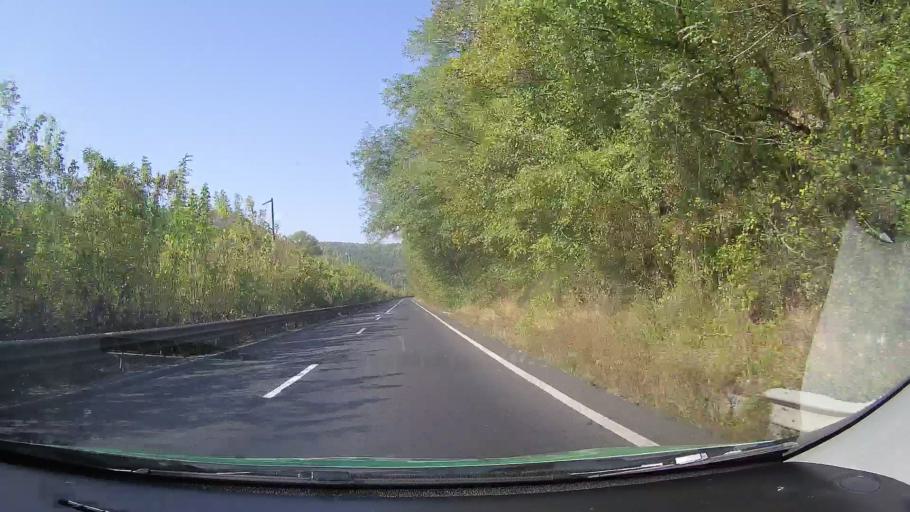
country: RO
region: Hunedoara
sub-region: Comuna Zam
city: Zam
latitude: 45.9747
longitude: 22.4377
